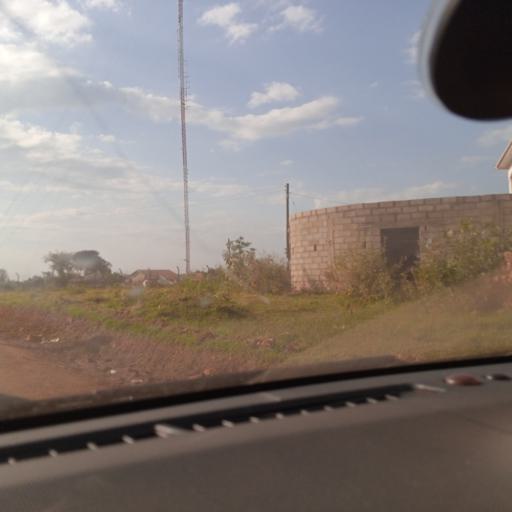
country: UG
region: Central Region
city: Masaka
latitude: -0.3618
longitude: 31.7480
